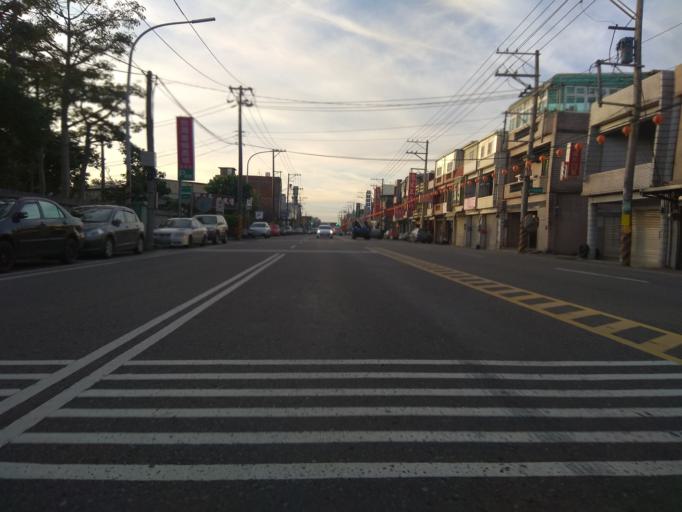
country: TW
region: Taiwan
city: Taoyuan City
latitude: 24.9943
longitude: 121.1660
